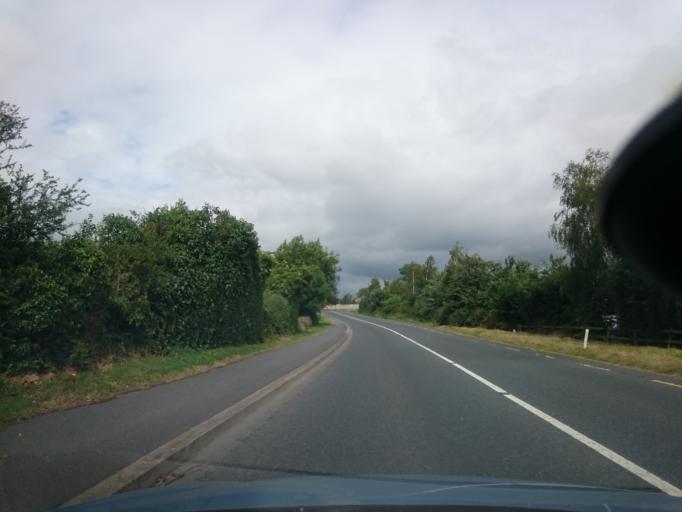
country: IE
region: Leinster
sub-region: County Carlow
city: Carlow
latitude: 52.8480
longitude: -6.8982
